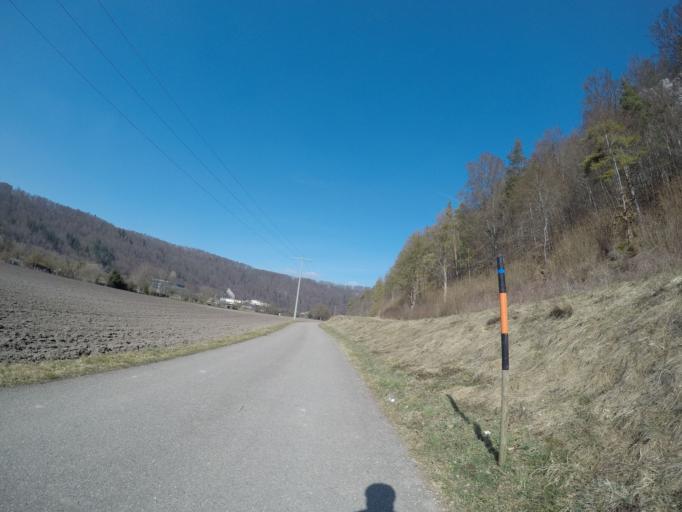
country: DE
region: Baden-Wuerttemberg
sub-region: Tuebingen Region
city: Blaubeuren
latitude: 48.3956
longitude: 9.7719
